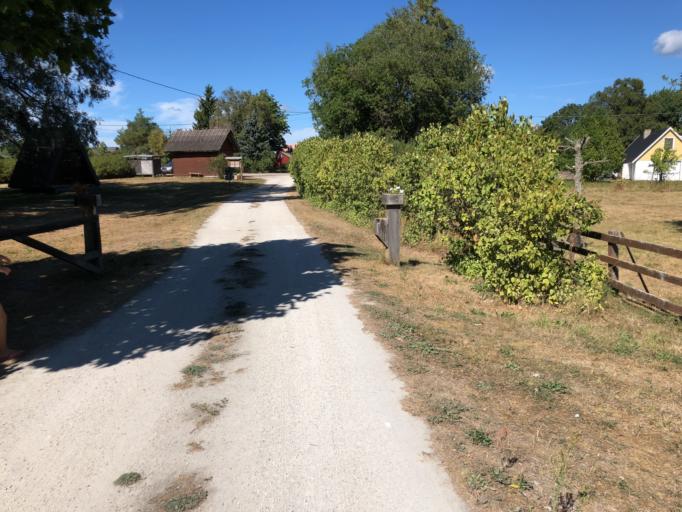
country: EE
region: Laeaene
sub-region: Haapsalu linn
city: Haapsalu
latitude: 58.7726
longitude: 23.5478
